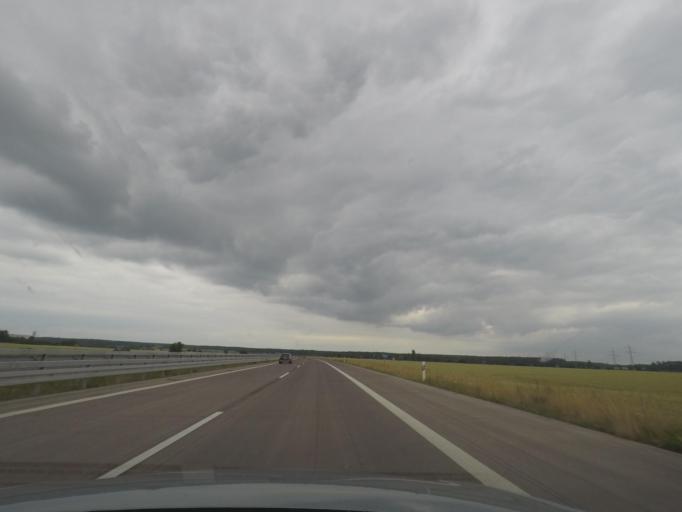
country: DE
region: Saxony-Anhalt
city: Colbitz
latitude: 52.3174
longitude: 11.6296
